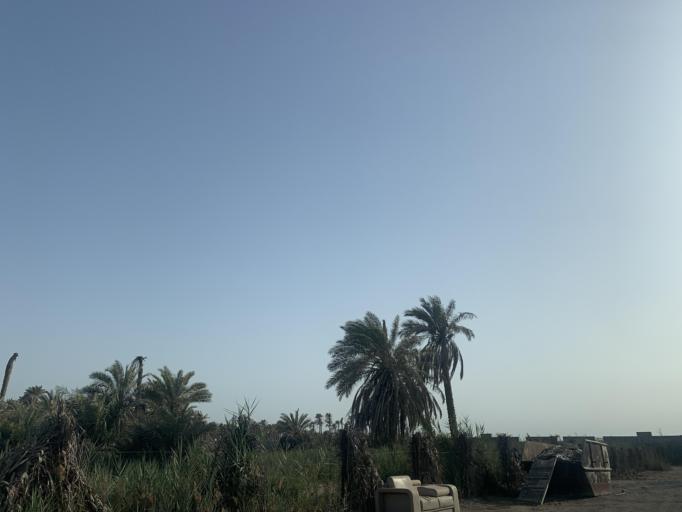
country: BH
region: Central Governorate
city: Madinat Hamad
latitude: 26.1875
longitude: 50.4583
